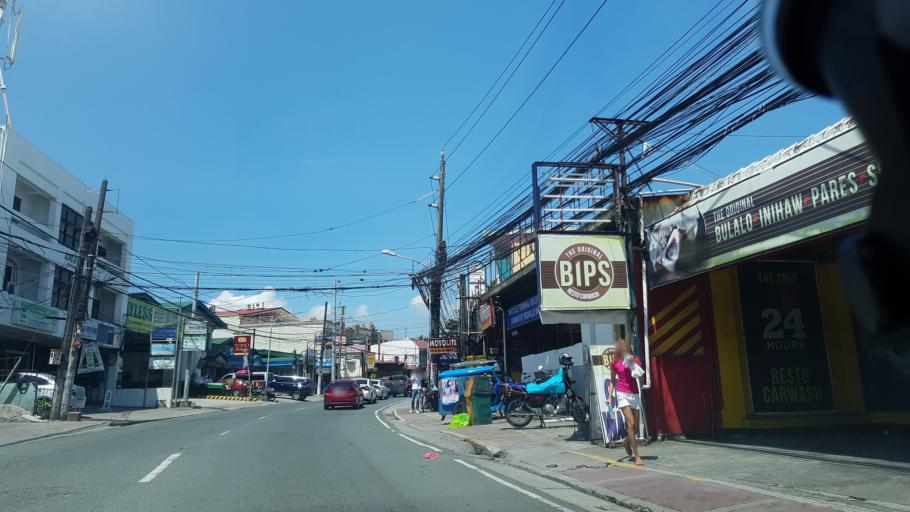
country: PH
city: Sambayanihan People's Village
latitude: 14.4568
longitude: 121.0311
